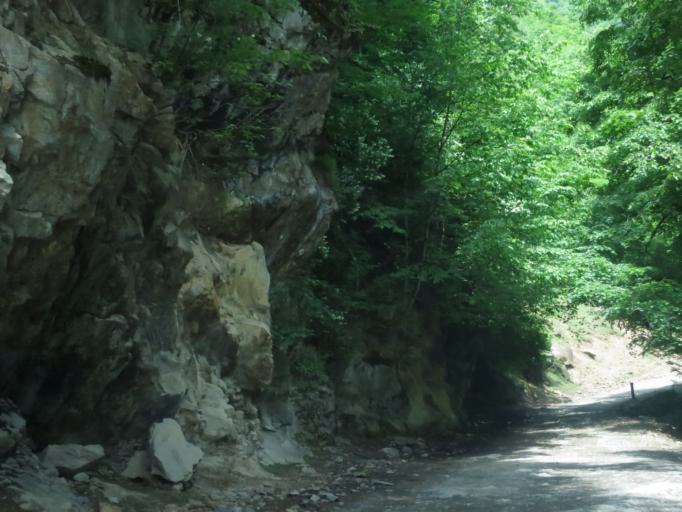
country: GE
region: Kakheti
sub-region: Telavi
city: Telavi
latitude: 42.2131
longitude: 45.4721
